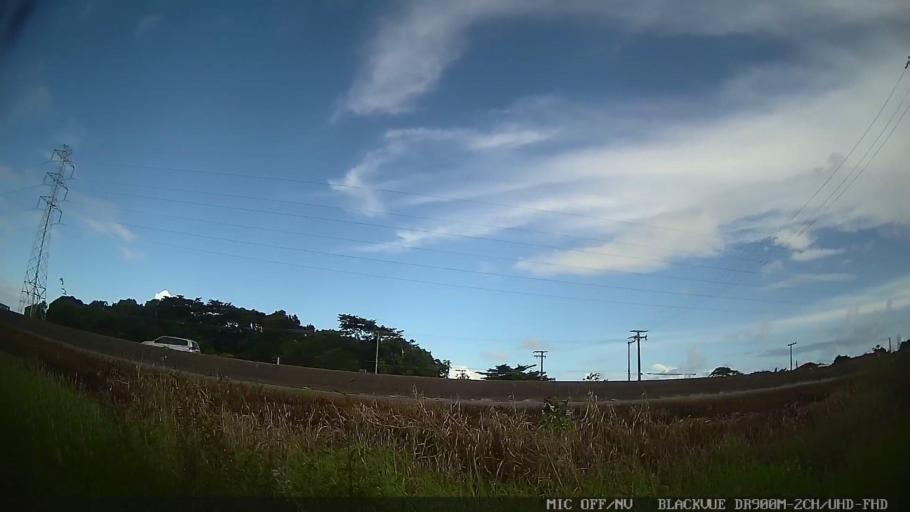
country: BR
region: Sao Paulo
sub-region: Itanhaem
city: Itanhaem
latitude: -24.2091
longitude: -46.8607
